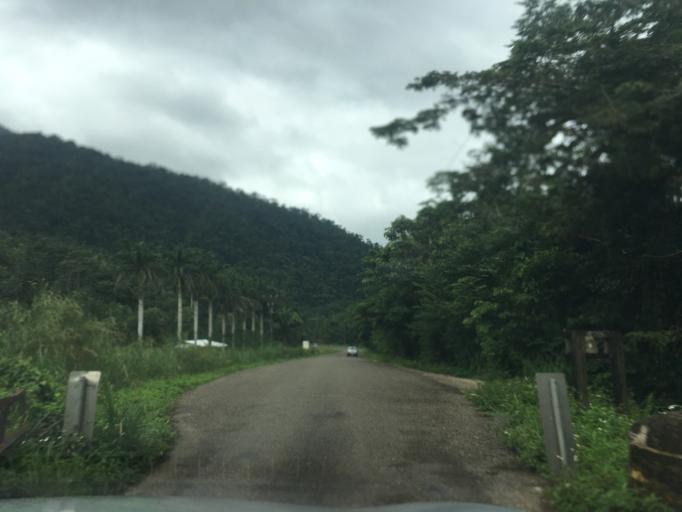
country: BZ
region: Cayo
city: Belmopan
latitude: 17.0559
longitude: -88.5808
